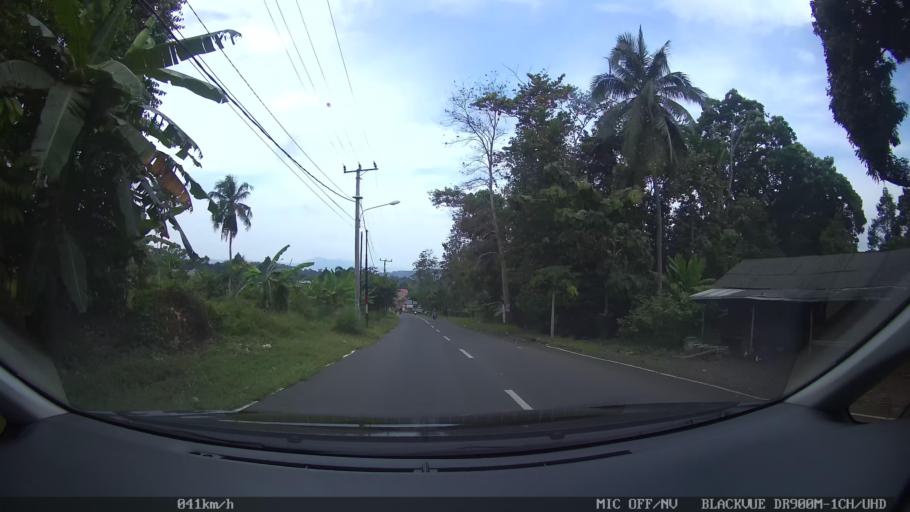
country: ID
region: Lampung
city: Bandarlampung
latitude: -5.4220
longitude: 105.1936
